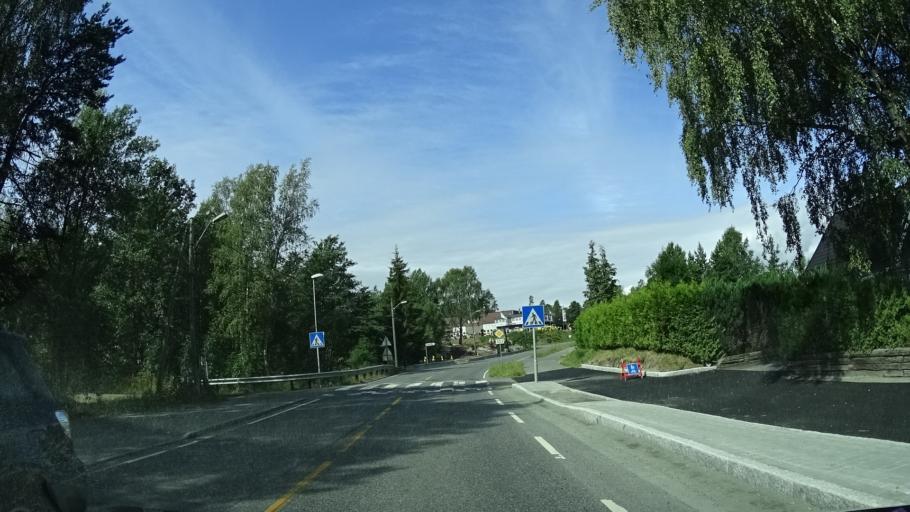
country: NO
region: Telemark
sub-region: Bamble
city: Langesund
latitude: 59.0432
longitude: 9.6700
